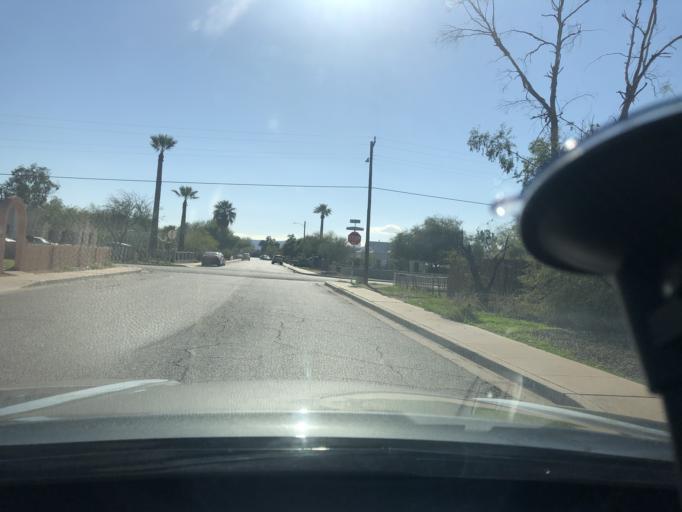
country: US
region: Arizona
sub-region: Maricopa County
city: Phoenix
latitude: 33.4721
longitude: -112.0290
